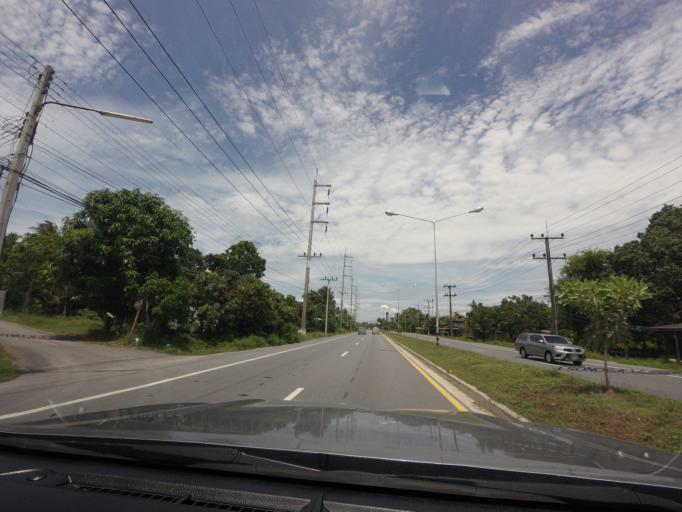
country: TH
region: Songkhla
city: Krasae Sin
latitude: 7.5823
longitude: 100.4068
